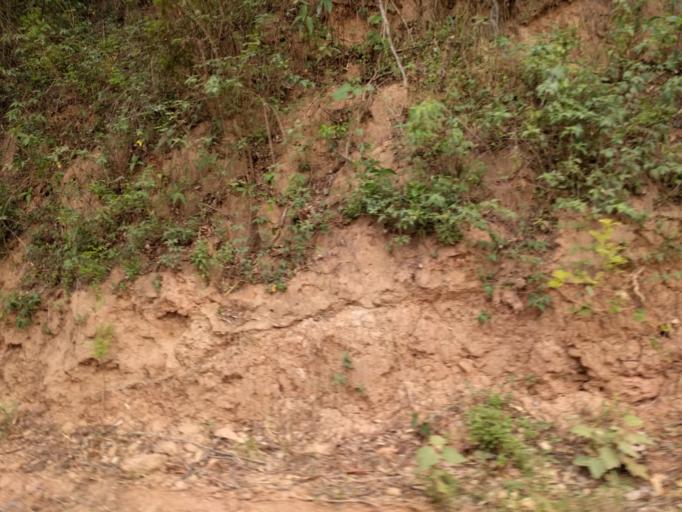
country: BO
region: Santa Cruz
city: Santiago del Torno
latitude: -17.9299
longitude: -63.4182
